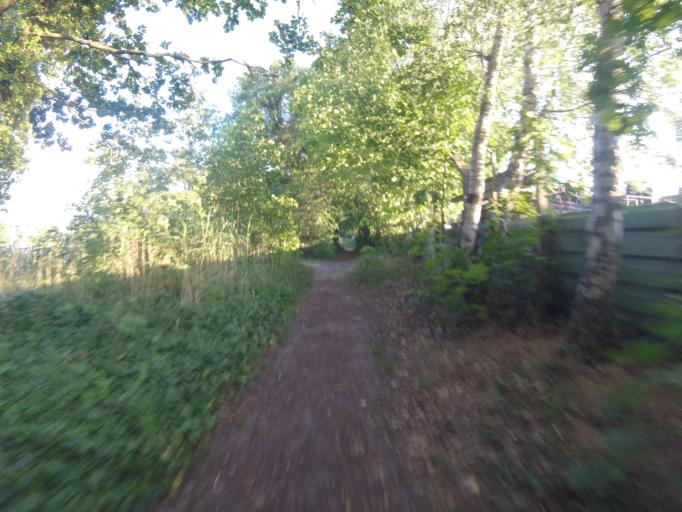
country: DE
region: Brandenburg
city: Mittenwalde
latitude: 52.2690
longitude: 13.5408
